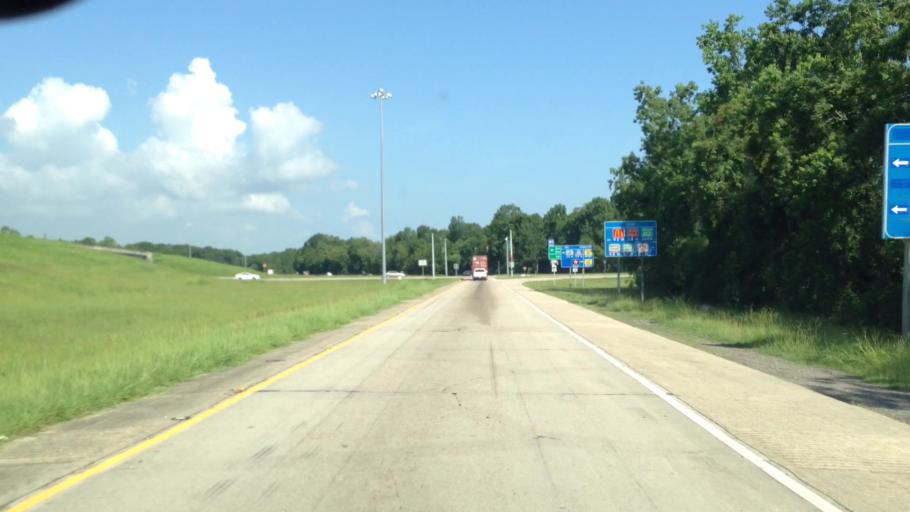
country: US
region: Louisiana
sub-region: Ascension Parish
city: Sorrento
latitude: 30.1715
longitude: -90.8743
